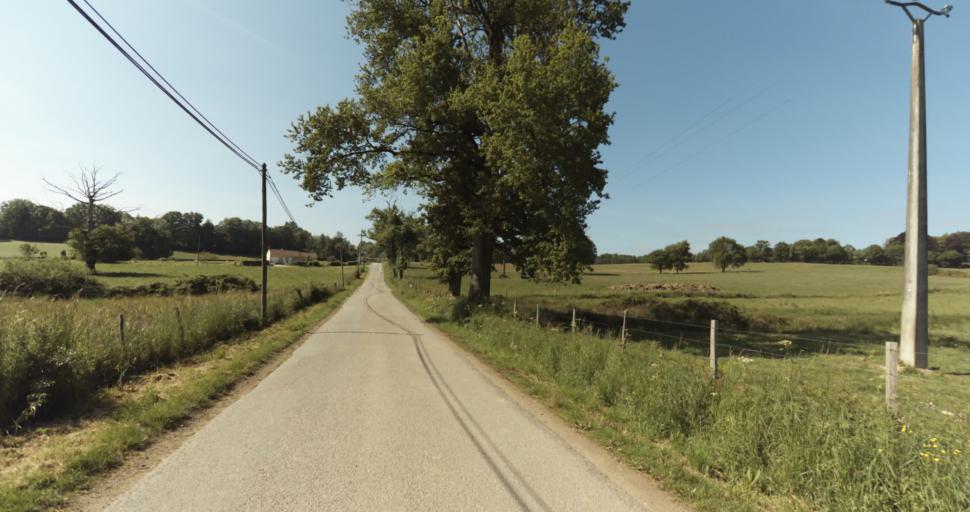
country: FR
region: Limousin
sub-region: Departement de la Haute-Vienne
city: Solignac
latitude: 45.7272
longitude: 1.2695
